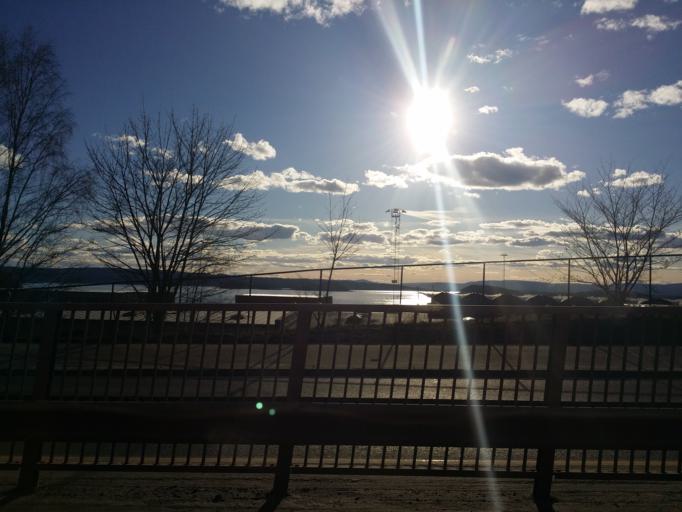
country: NO
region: Oslo
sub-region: Oslo
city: Oslo
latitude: 59.8849
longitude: 10.7686
